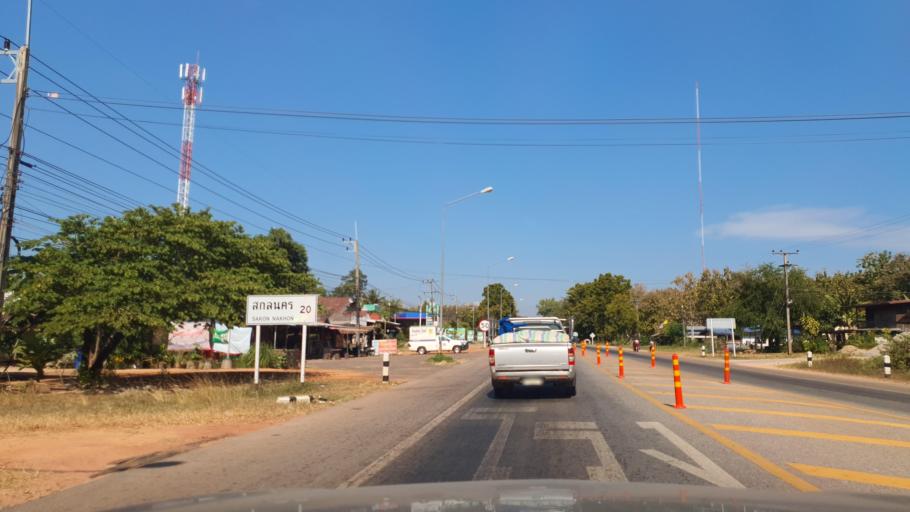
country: TH
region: Sakon Nakhon
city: Phu Phan
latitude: 17.0792
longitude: 103.9800
